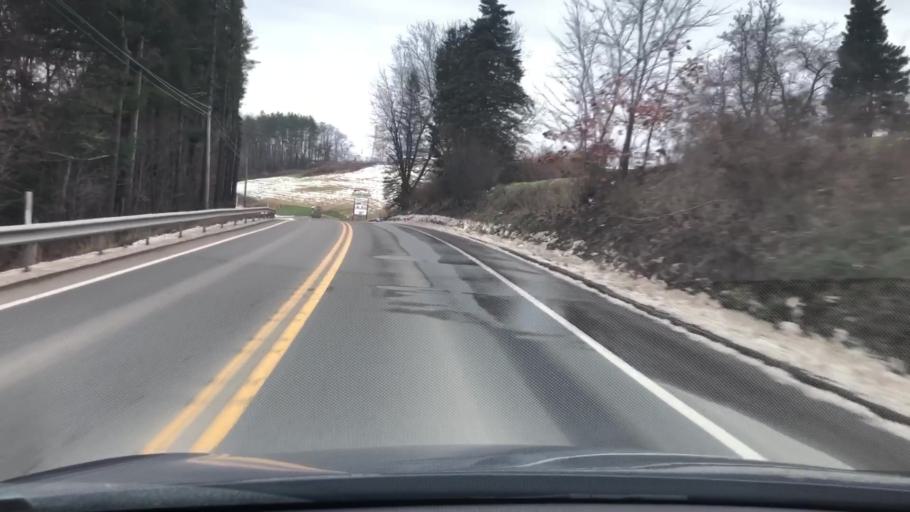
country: US
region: Pennsylvania
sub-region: Clarion County
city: Clarion
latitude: 41.0322
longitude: -79.2634
